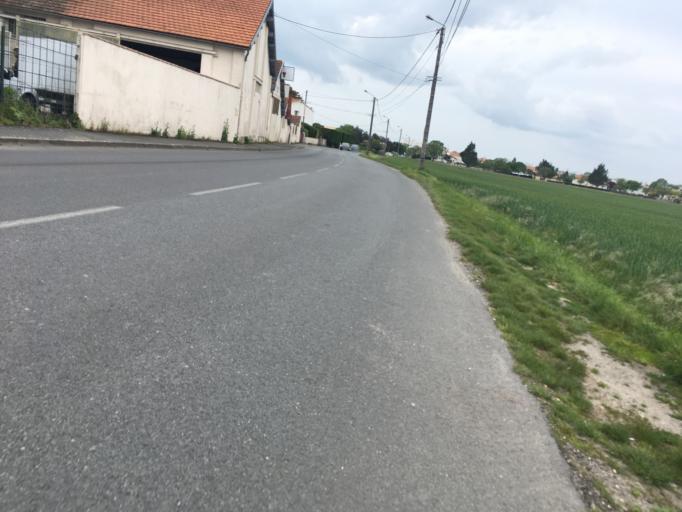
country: FR
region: Poitou-Charentes
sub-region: Departement de la Charente-Maritime
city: Aytre
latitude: 46.1415
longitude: -1.1232
